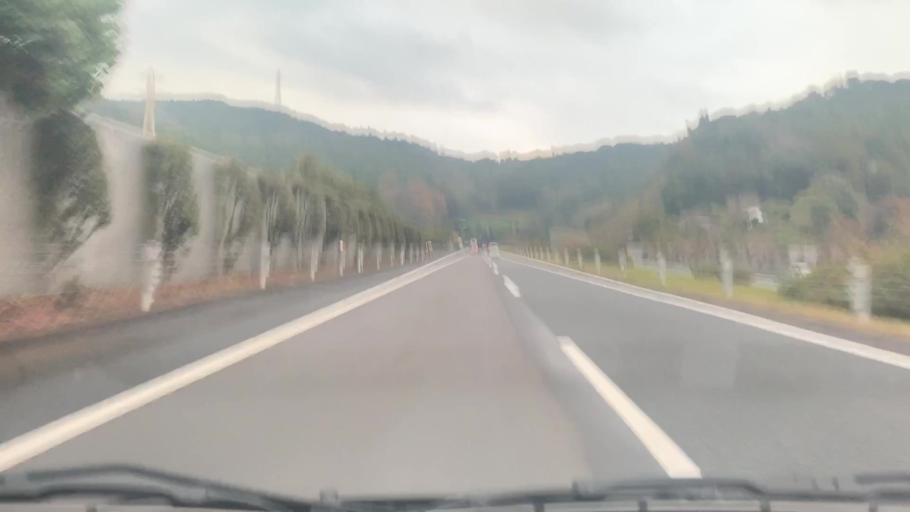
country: JP
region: Nagasaki
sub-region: Isahaya-shi
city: Isahaya
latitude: 32.8775
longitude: 129.9970
